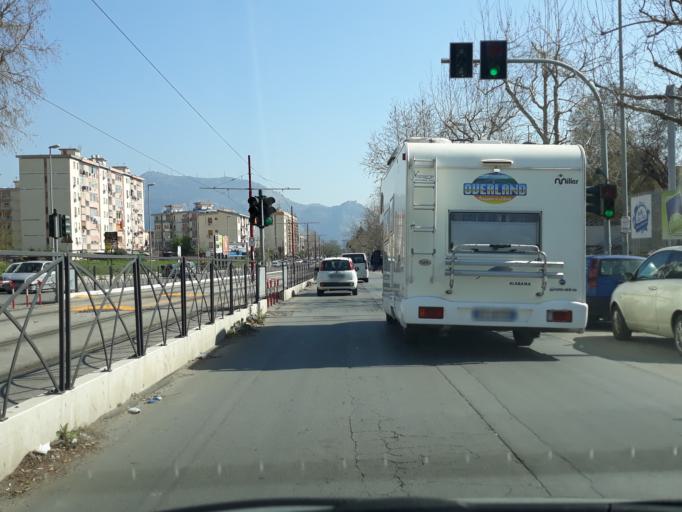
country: IT
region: Sicily
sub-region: Palermo
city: Palermo
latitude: 38.1321
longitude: 13.3072
